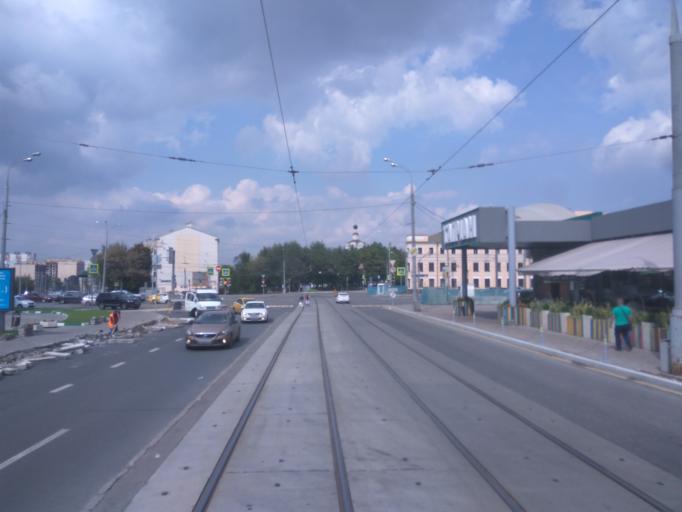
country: RU
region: Moscow
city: Taganskiy
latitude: 55.7459
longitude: 37.6703
